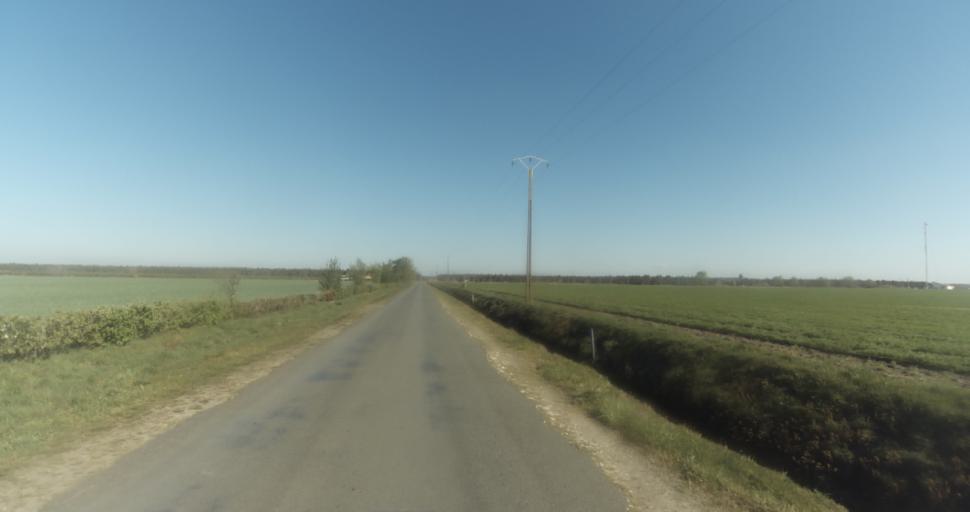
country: FR
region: Aquitaine
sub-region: Departement de la Gironde
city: Marcheprime
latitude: 44.7715
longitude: -0.8571
